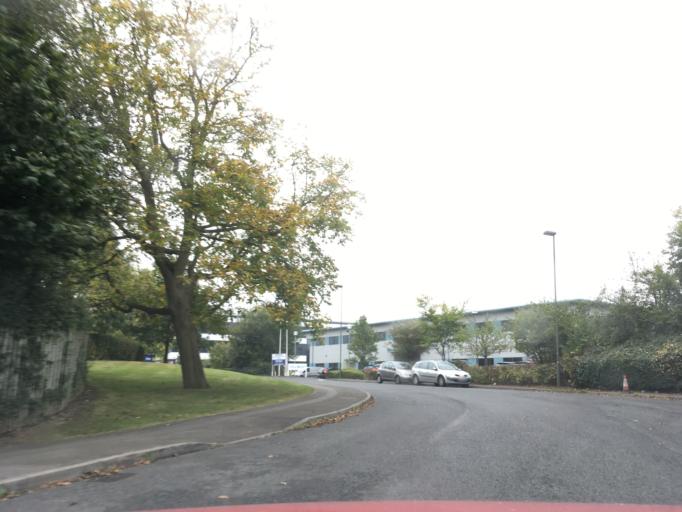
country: GB
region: England
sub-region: Gloucestershire
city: Stonehouse
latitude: 51.7541
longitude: -2.2941
